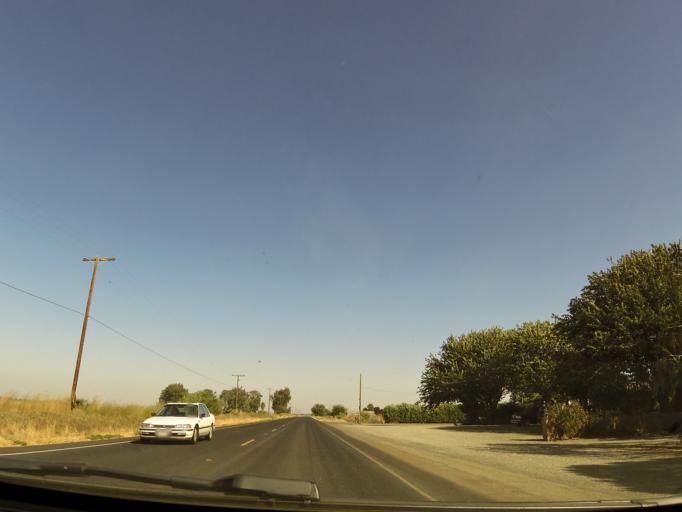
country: US
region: California
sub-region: San Joaquin County
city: Tracy
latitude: 37.8509
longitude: -121.4332
